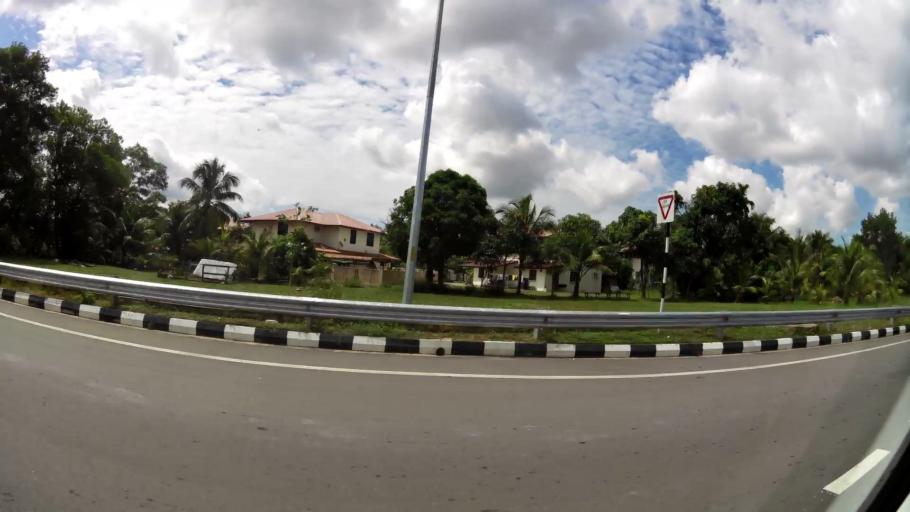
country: BN
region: Brunei and Muara
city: Bandar Seri Begawan
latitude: 4.9352
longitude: 114.8975
